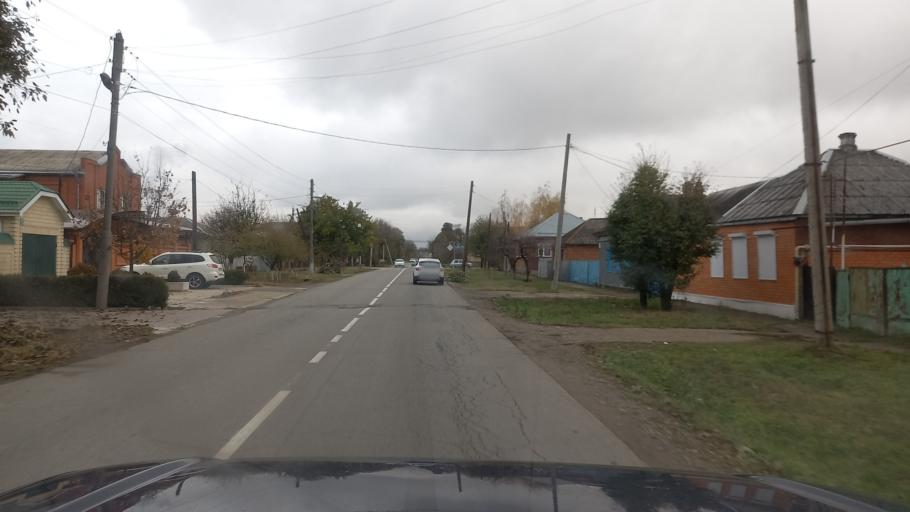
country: RU
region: Adygeya
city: Maykop
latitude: 44.6077
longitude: 40.0727
